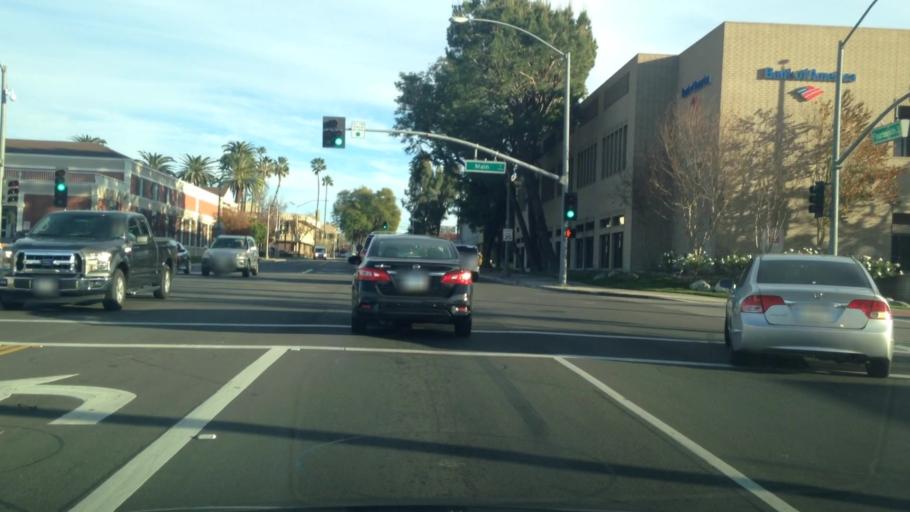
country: US
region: California
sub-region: Riverside County
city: Riverside
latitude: 33.9763
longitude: -117.3787
